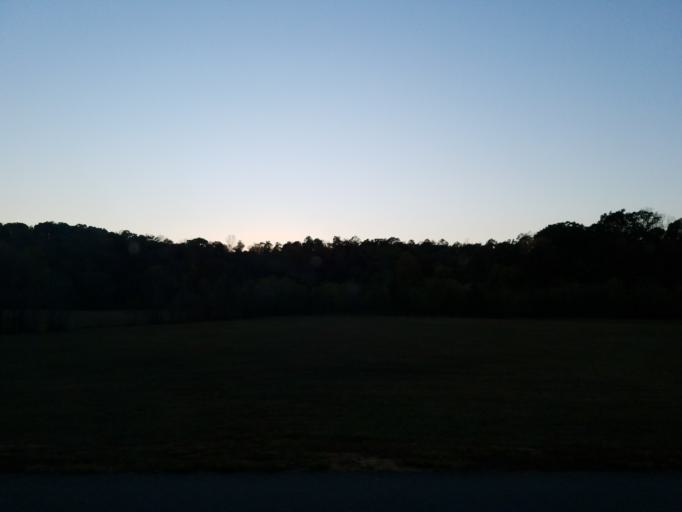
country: US
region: Georgia
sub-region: Gordon County
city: Calhoun
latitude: 34.5834
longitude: -84.9533
